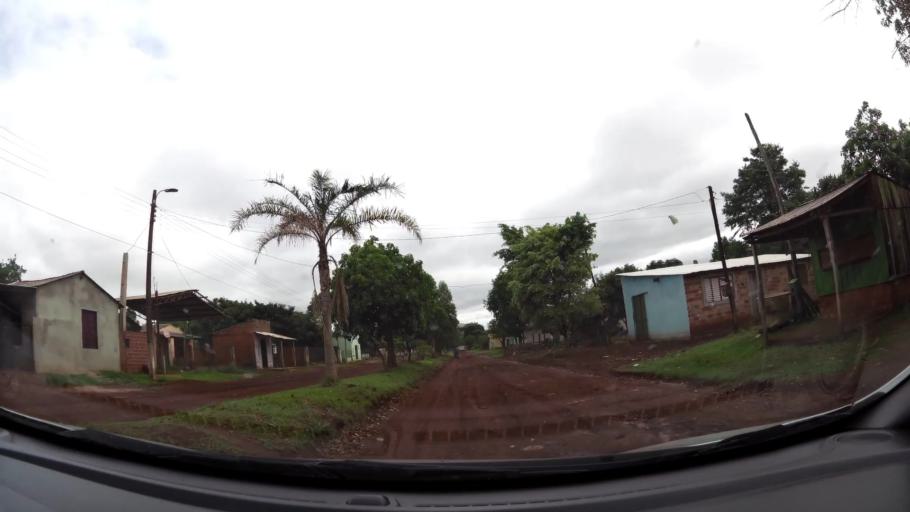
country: PY
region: Alto Parana
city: Ciudad del Este
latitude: -25.3719
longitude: -54.6479
